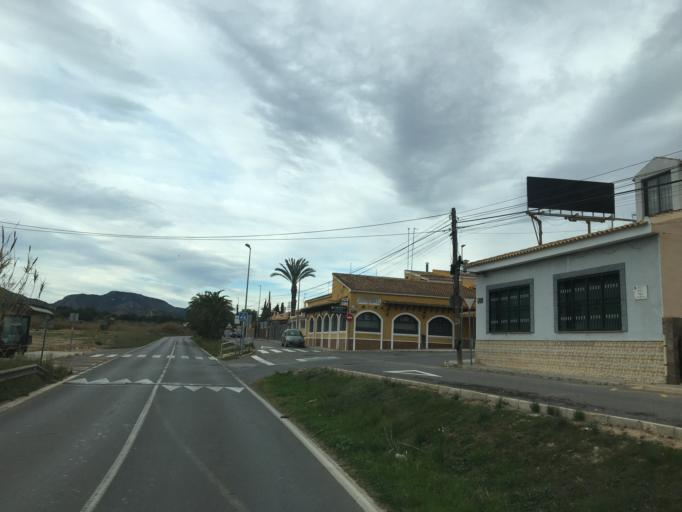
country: ES
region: Murcia
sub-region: Murcia
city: Cartagena
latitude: 37.6125
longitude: -1.0242
